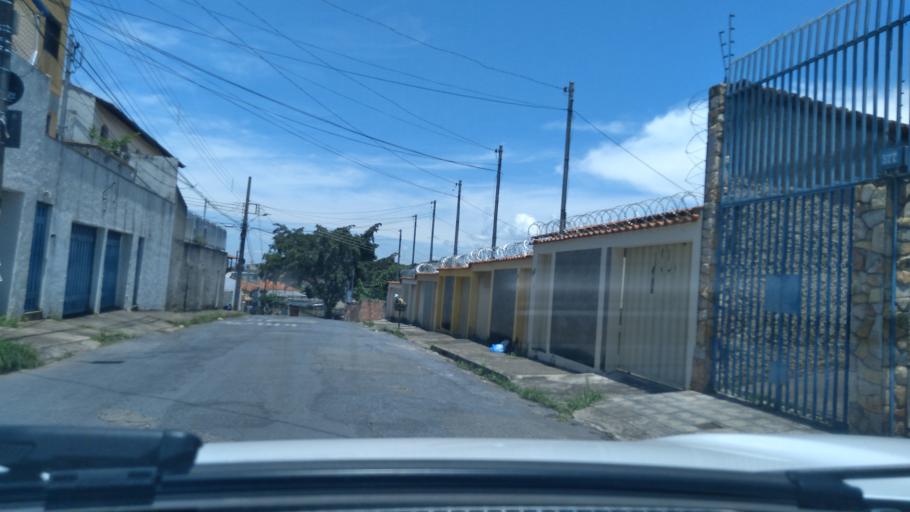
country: BR
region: Minas Gerais
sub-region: Contagem
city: Contagem
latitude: -19.9342
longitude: -43.9979
